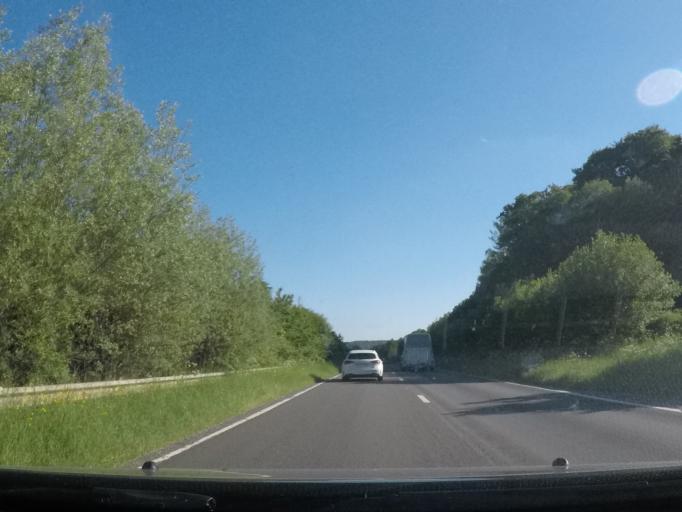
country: BE
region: Wallonia
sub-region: Province du Luxembourg
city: Saint-Hubert
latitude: 49.9792
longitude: 5.3744
